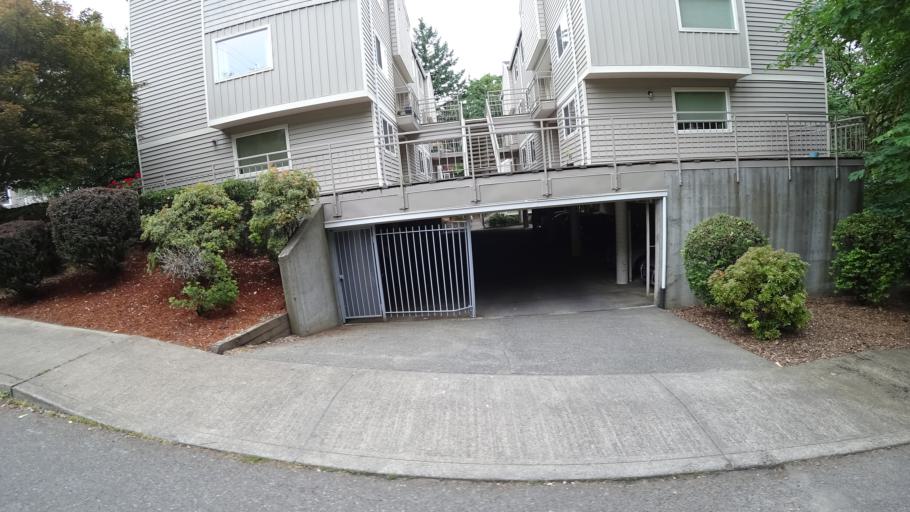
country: US
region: Oregon
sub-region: Multnomah County
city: Portland
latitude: 45.4968
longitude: -122.6923
